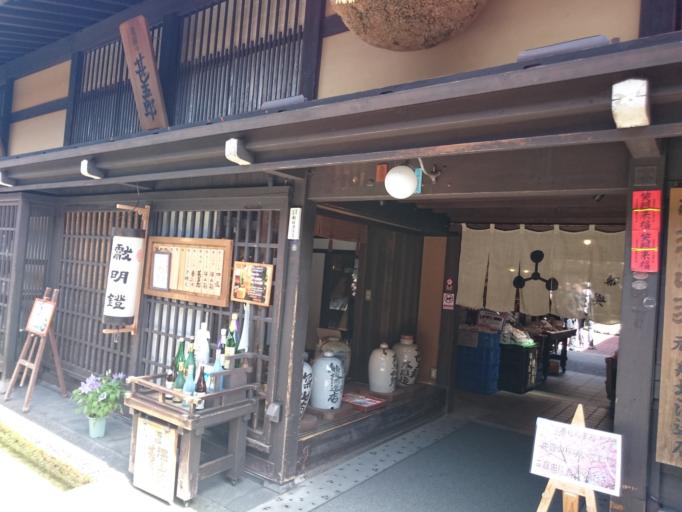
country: JP
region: Gifu
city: Takayama
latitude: 36.1407
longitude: 137.2596
